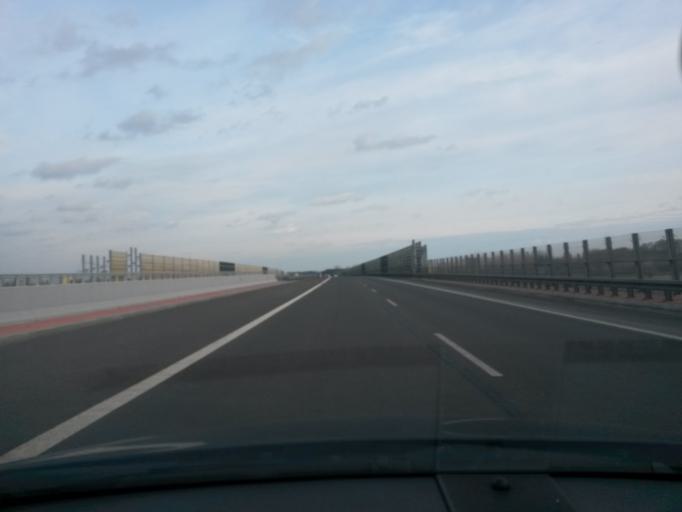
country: PL
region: Greater Poland Voivodeship
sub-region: Powiat turecki
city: Brudzew
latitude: 52.1219
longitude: 18.6893
